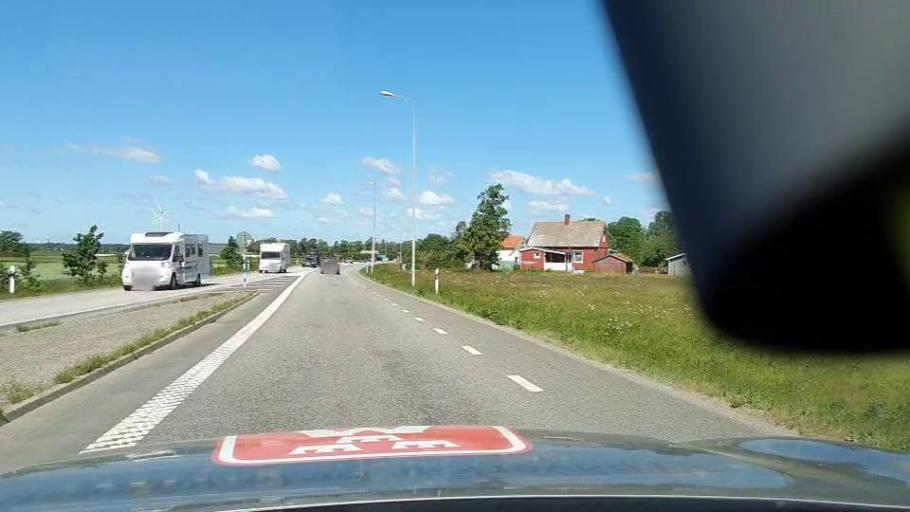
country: SE
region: Blekinge
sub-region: Solvesborgs Kommun
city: Soelvesborg
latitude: 56.0447
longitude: 14.6660
